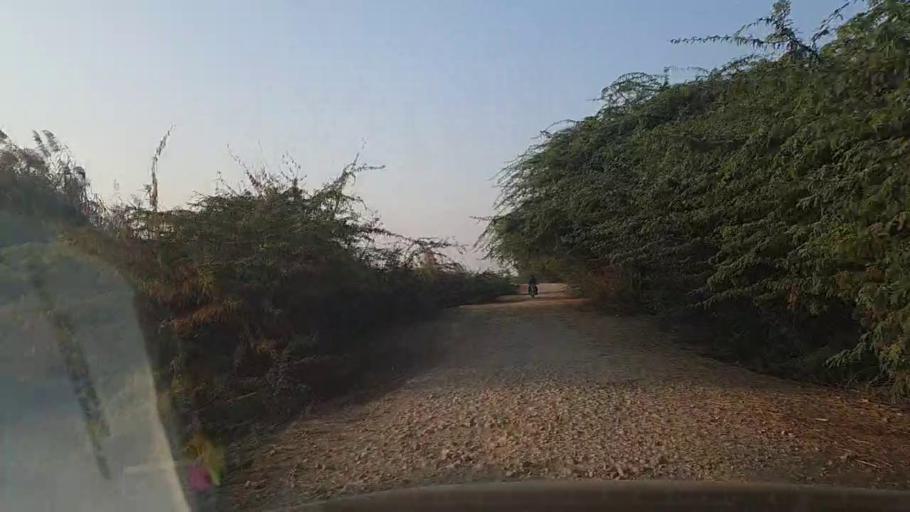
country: PK
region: Sindh
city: Keti Bandar
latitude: 24.3140
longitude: 67.5997
